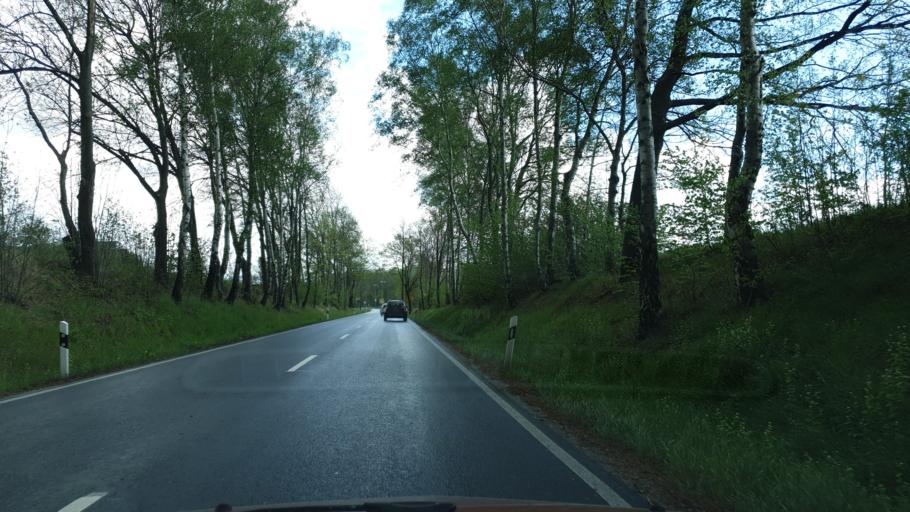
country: DE
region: Saxony
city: Neukirchen
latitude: 50.8051
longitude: 12.8386
